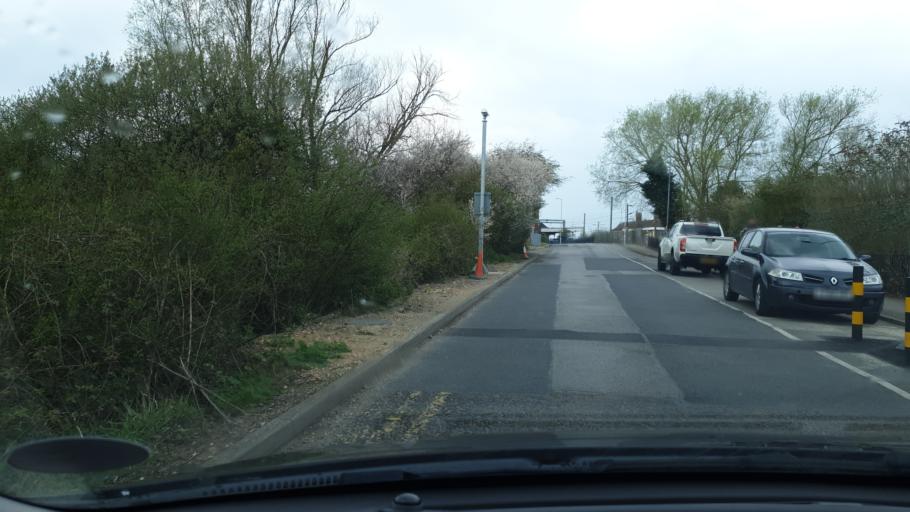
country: GB
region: England
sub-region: Essex
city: Manningtree
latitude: 51.9488
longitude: 1.0477
